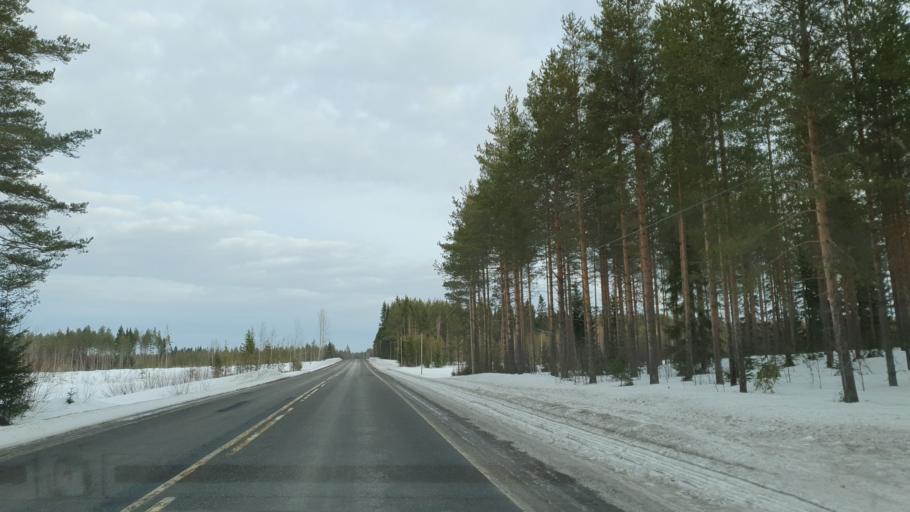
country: FI
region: Kainuu
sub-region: Kajaani
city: Vuokatti
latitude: 64.1863
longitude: 28.1841
